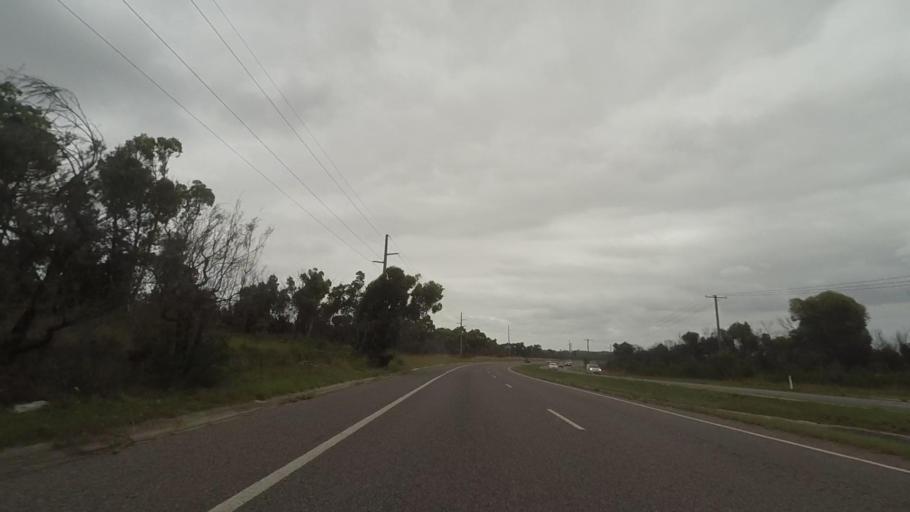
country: AU
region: New South Wales
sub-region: Wyong Shire
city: Kingfisher Shores
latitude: -33.1837
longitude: 151.5915
